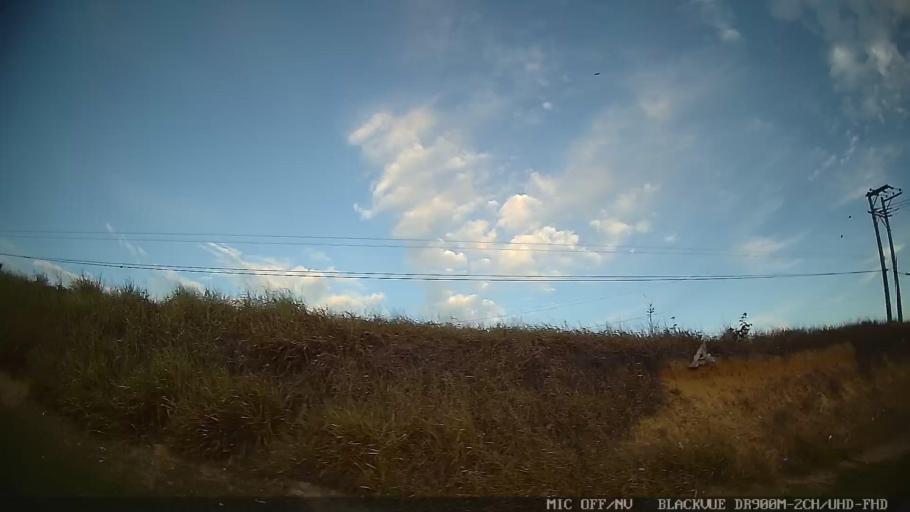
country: BR
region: Sao Paulo
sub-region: Salto
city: Salto
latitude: -23.1732
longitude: -47.2698
